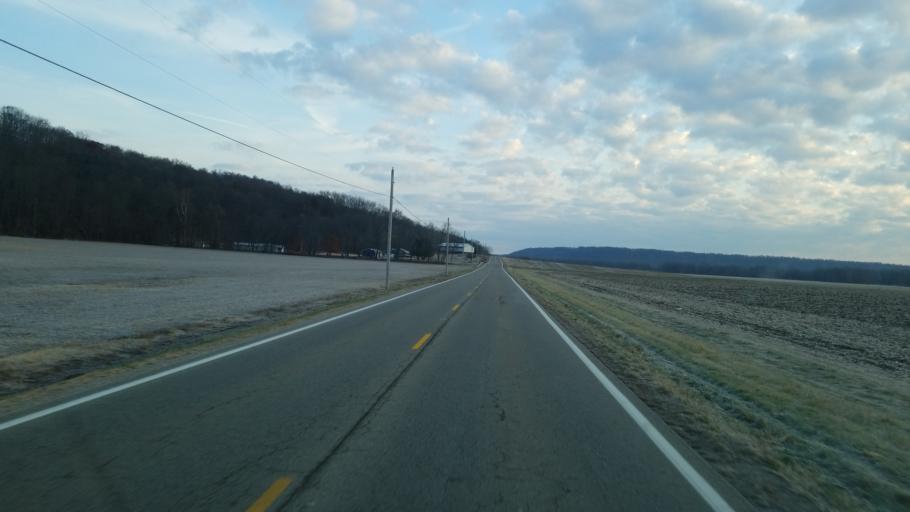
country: US
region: Ohio
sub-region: Ross County
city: Frankfort
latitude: 39.2571
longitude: -83.1871
